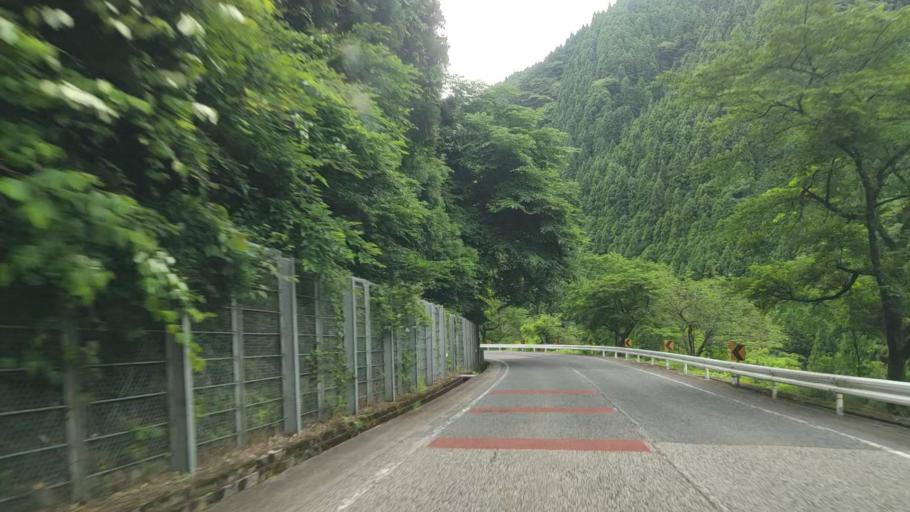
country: JP
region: Tottori
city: Yonago
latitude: 35.2533
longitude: 133.4388
